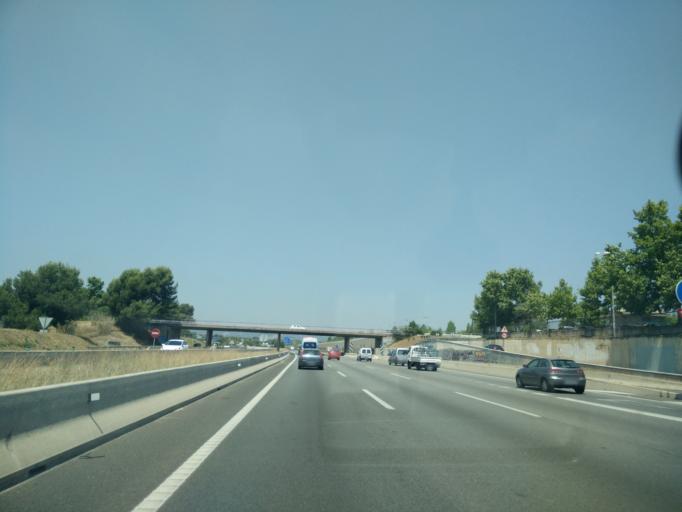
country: ES
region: Catalonia
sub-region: Provincia de Barcelona
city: Sant Quirze del Valles
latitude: 41.5367
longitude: 2.0876
